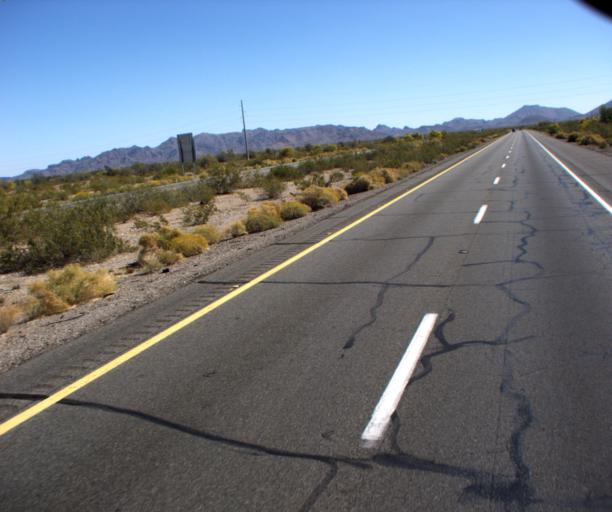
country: US
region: Arizona
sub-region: La Paz County
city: Quartzsite
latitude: 33.6690
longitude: -114.1679
